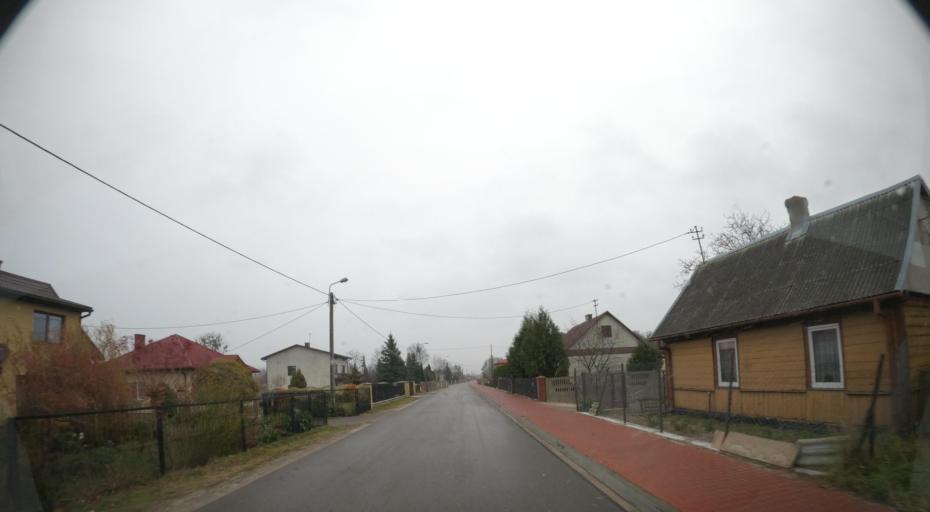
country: PL
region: Masovian Voivodeship
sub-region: Powiat radomski
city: Jedlnia-Letnisko
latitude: 51.4169
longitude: 21.2778
